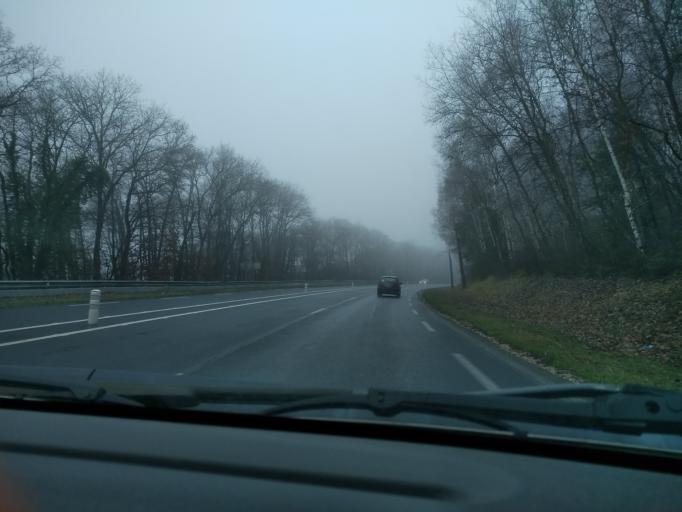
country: FR
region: Centre
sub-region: Departement d'Eure-et-Loir
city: Marboue
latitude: 48.1199
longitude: 1.3304
